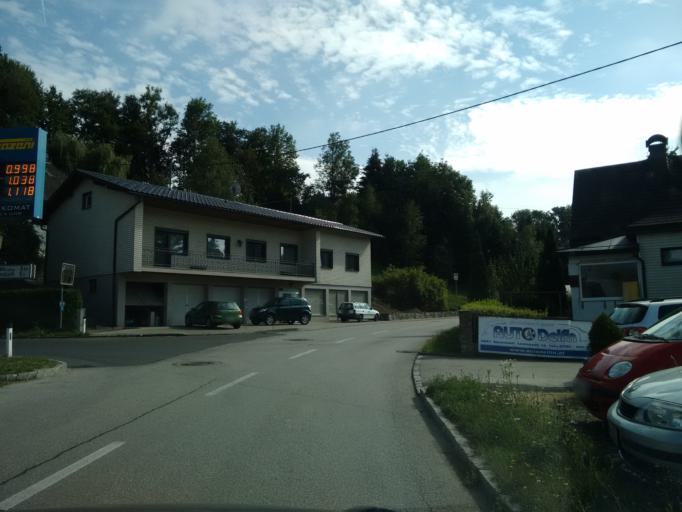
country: AT
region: Upper Austria
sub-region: Wels-Land
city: Marchtrenk
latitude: 48.1237
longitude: 14.0936
